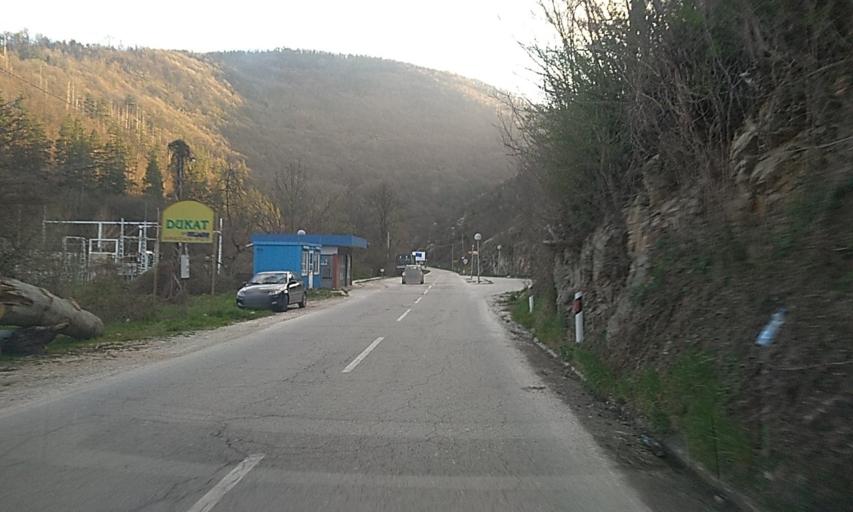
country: RS
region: Central Serbia
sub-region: Pcinjski Okrug
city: Bosilegrad
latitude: 42.4998
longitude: 22.4679
